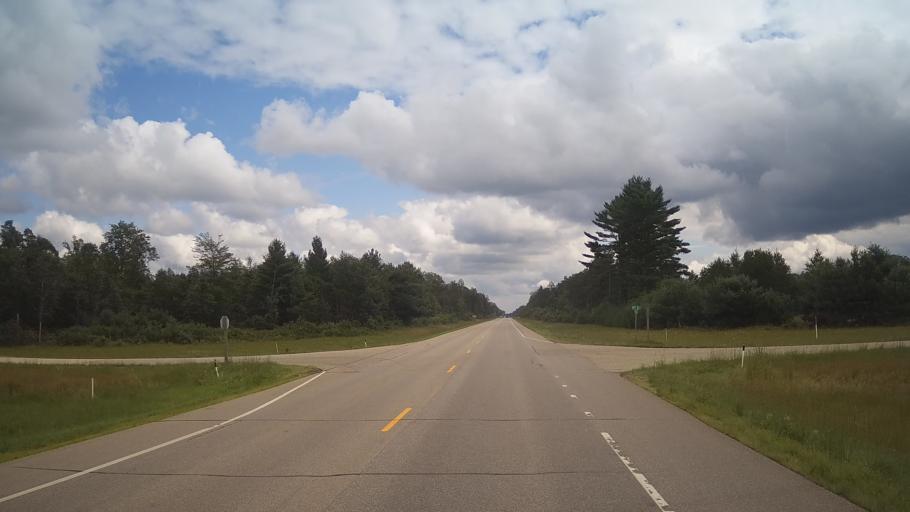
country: US
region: Wisconsin
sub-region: Adams County
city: Friendship
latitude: 44.0251
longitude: -89.7486
